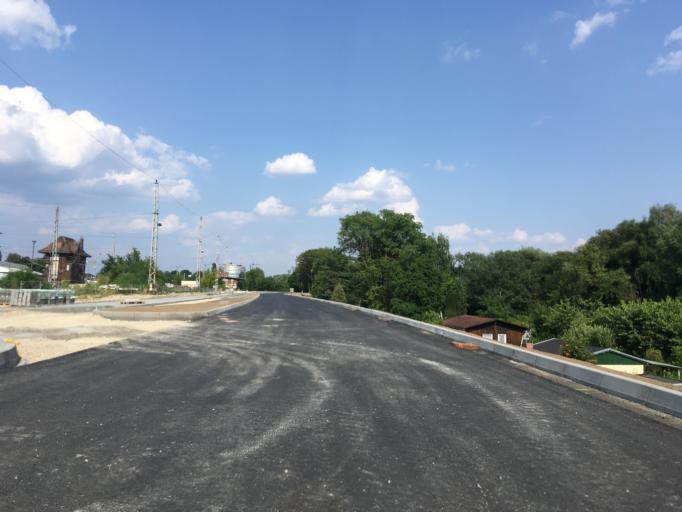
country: DE
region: Brandenburg
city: Bernau bei Berlin
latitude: 52.6735
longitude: 13.5881
